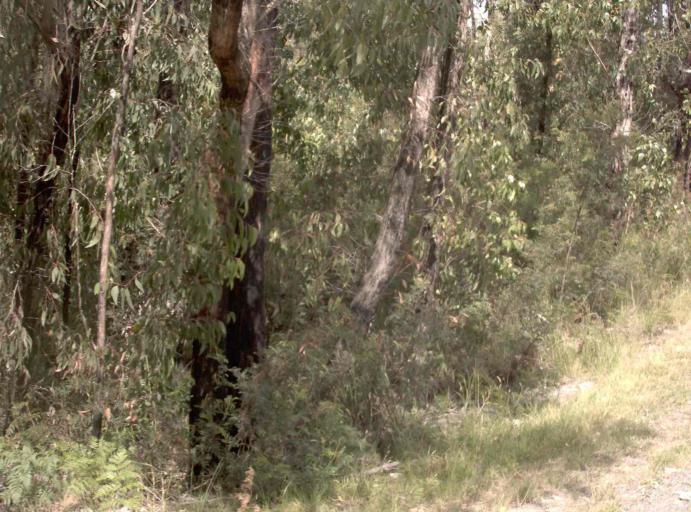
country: AU
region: Victoria
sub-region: Latrobe
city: Traralgon
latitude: -38.3135
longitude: 146.5656
